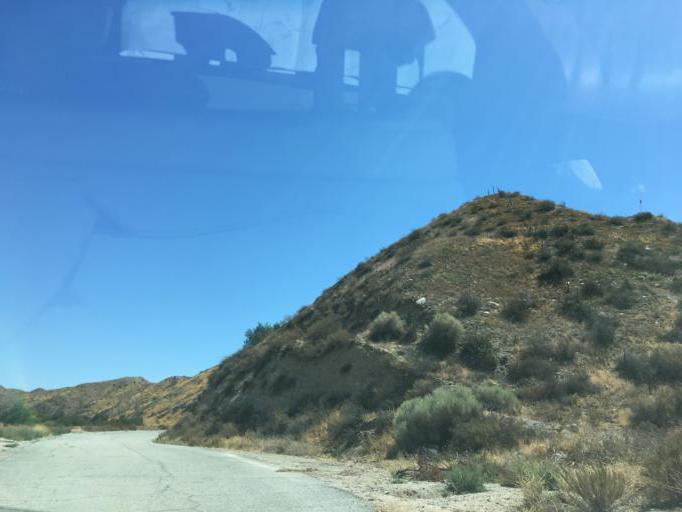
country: US
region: California
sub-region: Los Angeles County
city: Agua Dulce
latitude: 34.4361
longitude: -118.3787
